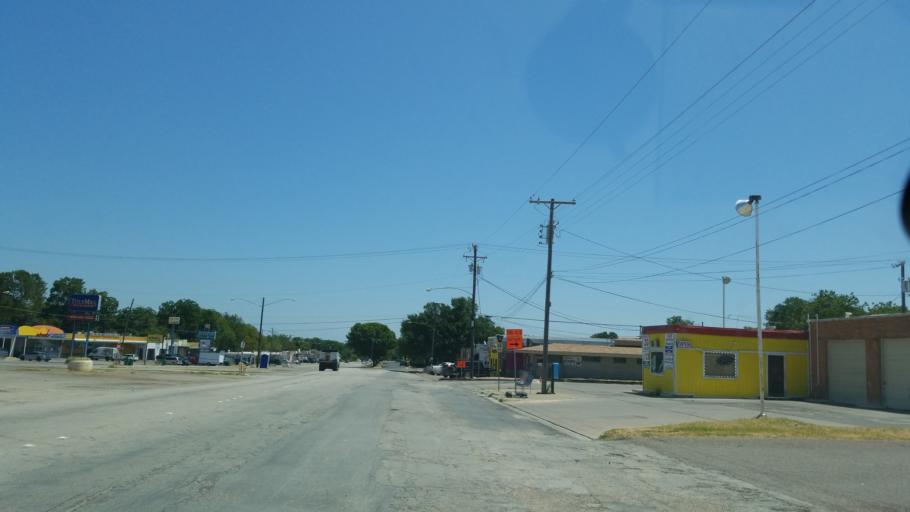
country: US
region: Texas
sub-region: Dallas County
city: Cockrell Hill
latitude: 32.7376
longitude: -96.8893
